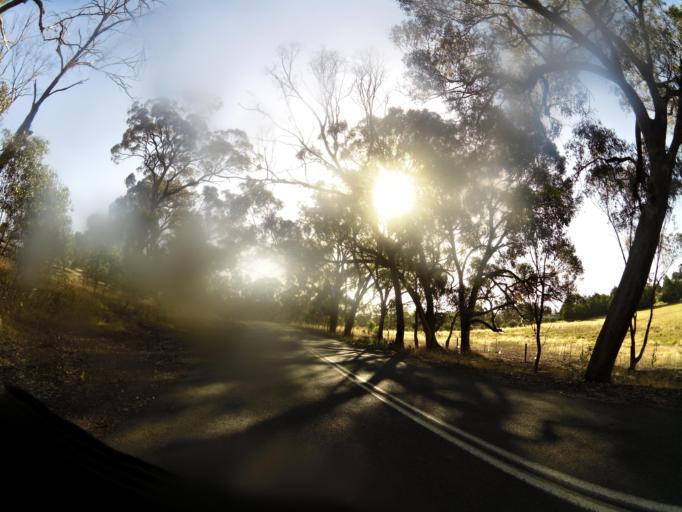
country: AU
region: Victoria
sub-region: Murrindindi
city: Kinglake West
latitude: -37.0115
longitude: 145.1200
